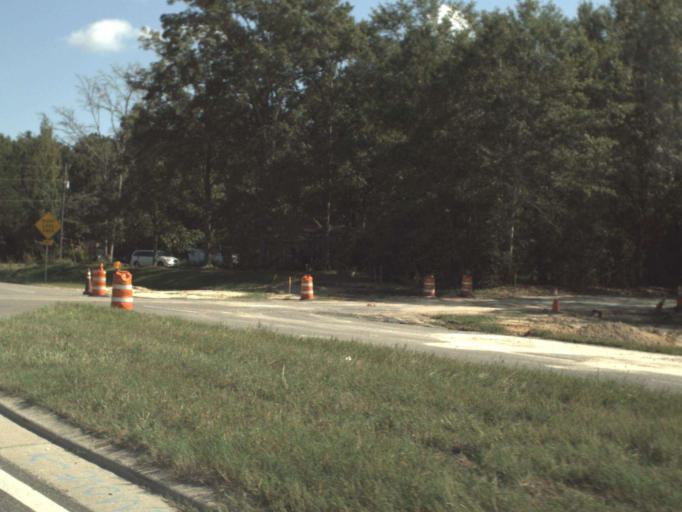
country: US
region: Florida
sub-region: Walton County
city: Freeport
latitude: 30.4880
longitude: -86.1225
